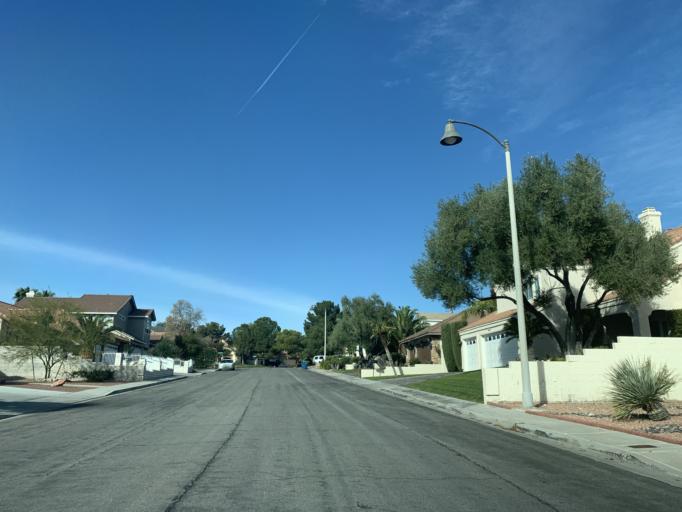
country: US
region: Nevada
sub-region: Clark County
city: Summerlin South
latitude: 36.1313
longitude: -115.2861
